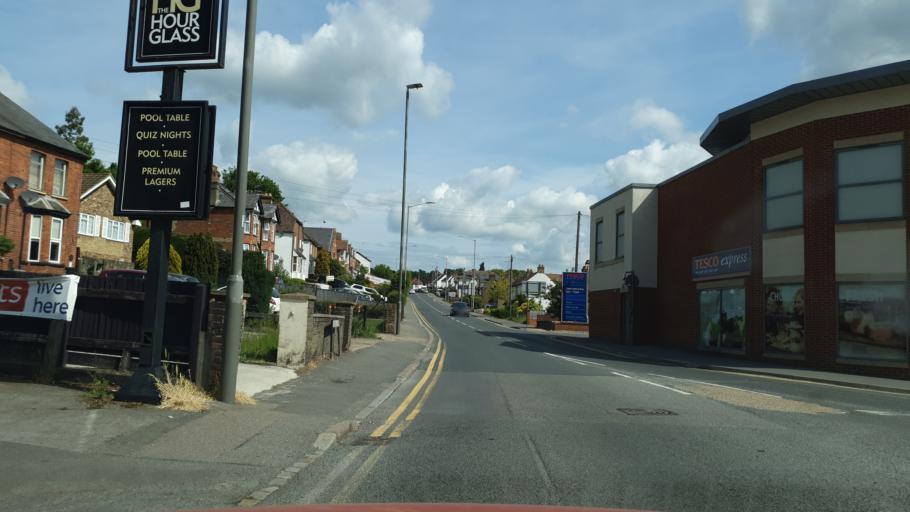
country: GB
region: England
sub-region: Buckinghamshire
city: High Wycombe
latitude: 51.6329
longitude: -0.7844
